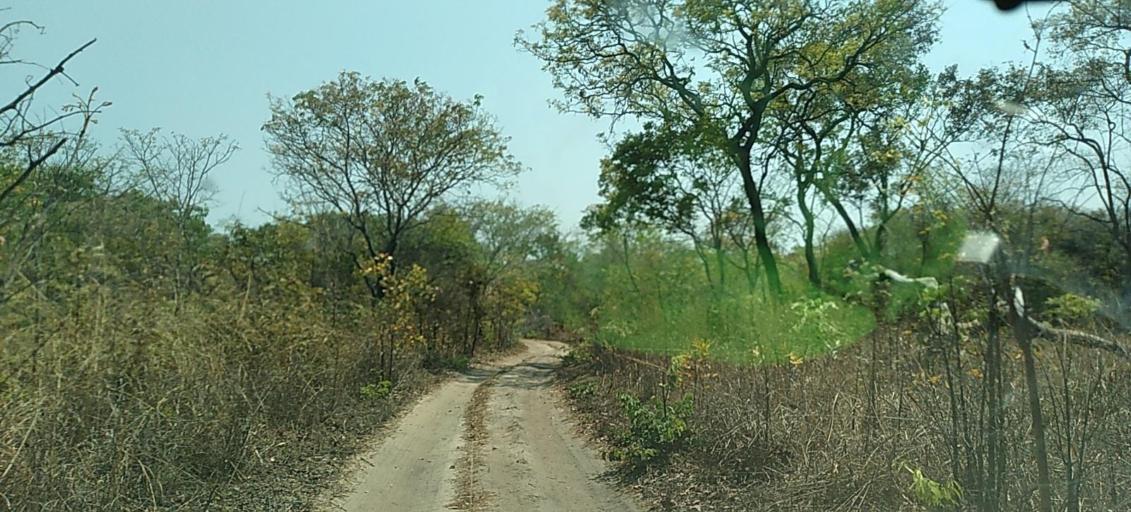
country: ZM
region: North-Western
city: Kalengwa
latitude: -13.1110
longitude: 24.6907
